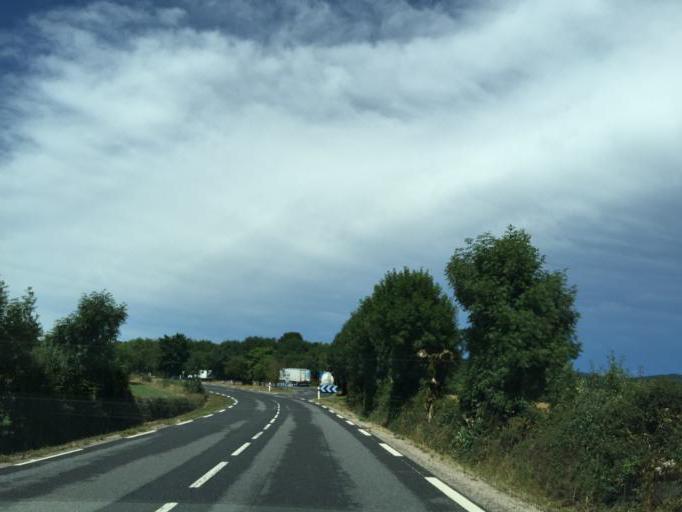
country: FR
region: Midi-Pyrenees
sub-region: Departement de l'Aveyron
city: Severac-le-Chateau
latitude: 44.2240
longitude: 2.9941
